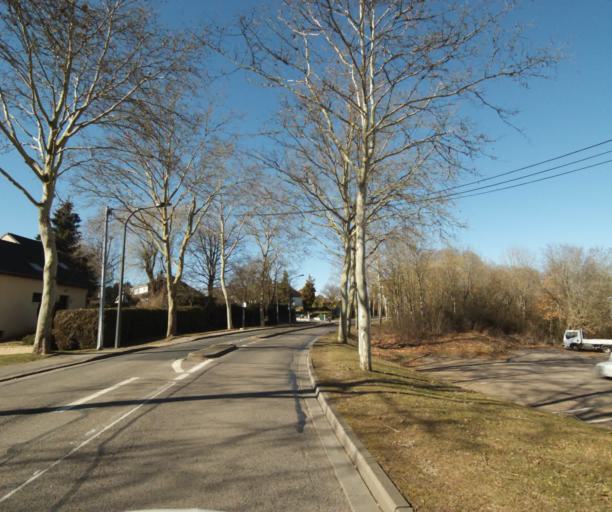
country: FR
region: Lorraine
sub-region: Departement de Meurthe-et-Moselle
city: Heillecourt
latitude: 48.6529
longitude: 6.2035
